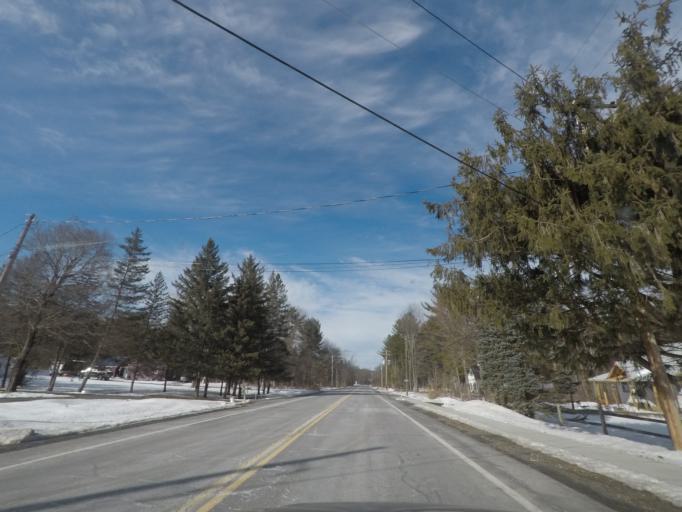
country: US
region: New York
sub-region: Albany County
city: Voorheesville
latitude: 42.6537
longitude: -73.9386
